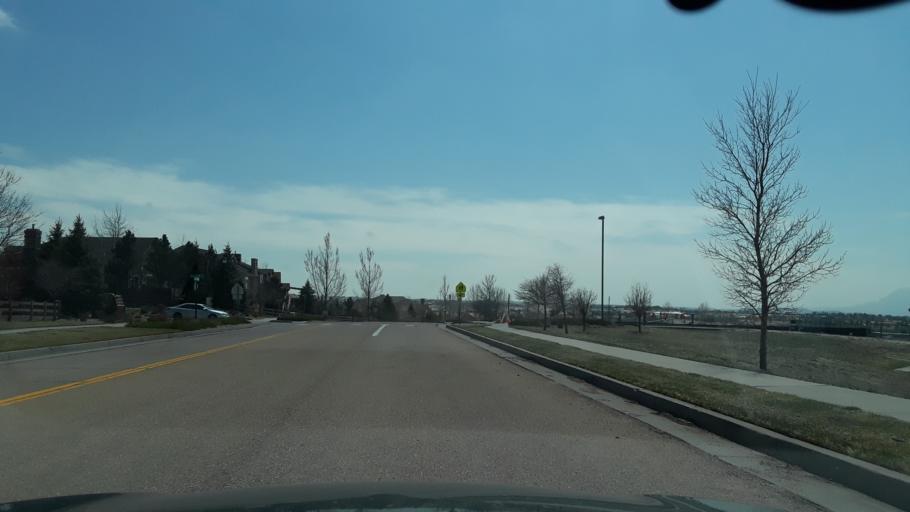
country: US
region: Colorado
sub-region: El Paso County
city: Gleneagle
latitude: 39.0326
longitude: -104.7909
